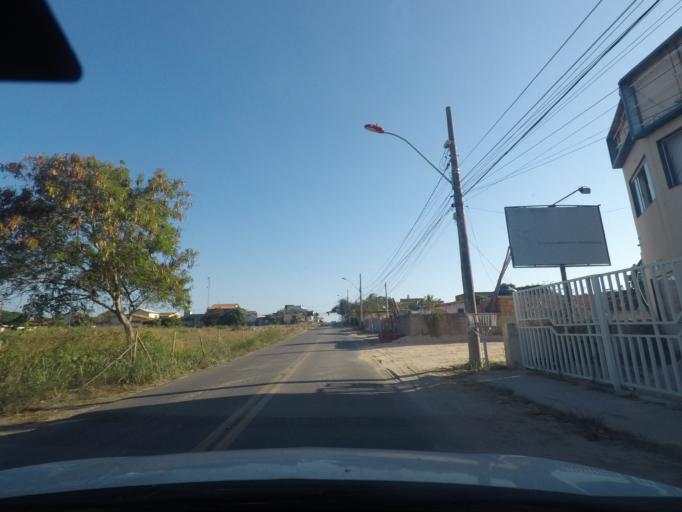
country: BR
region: Rio de Janeiro
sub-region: Marica
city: Marica
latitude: -22.9654
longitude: -42.9424
